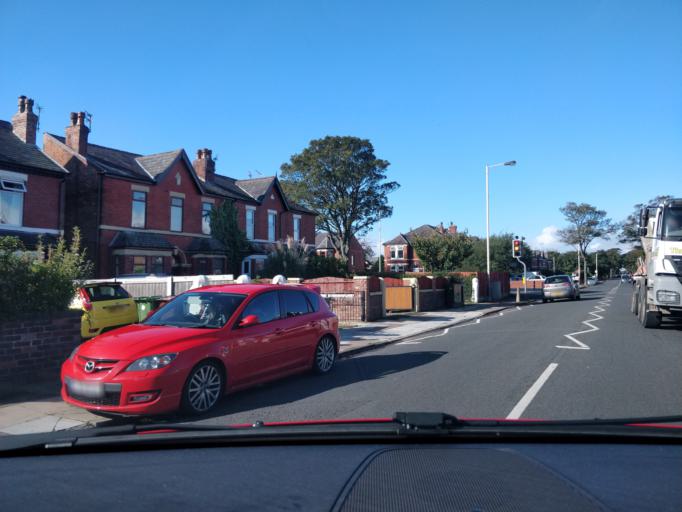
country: GB
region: England
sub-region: Sefton
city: Southport
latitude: 53.6428
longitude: -2.9774
